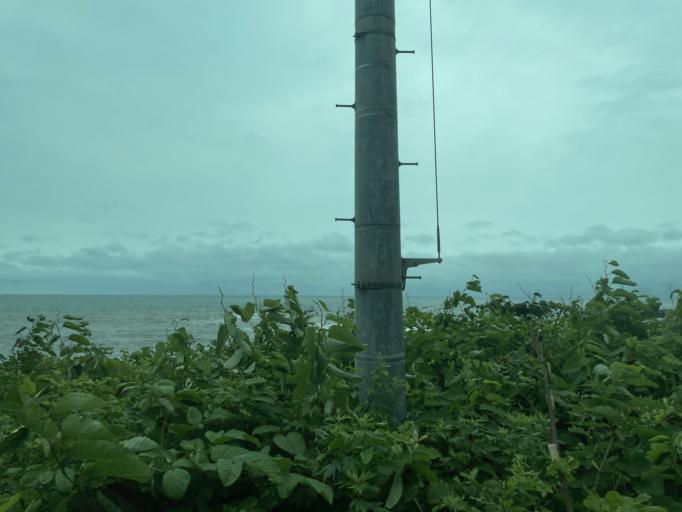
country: JP
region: Aomori
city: Shimokizukuri
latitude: 40.6984
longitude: 139.9694
